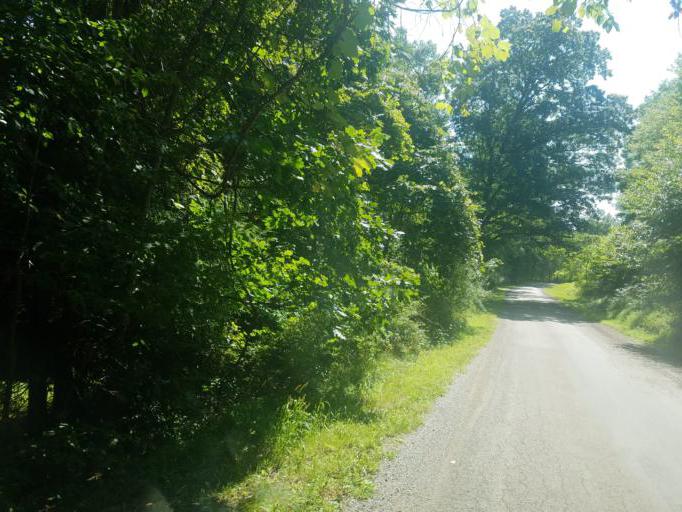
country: US
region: Pennsylvania
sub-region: Clarion County
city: Clarion
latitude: 41.1749
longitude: -79.4294
